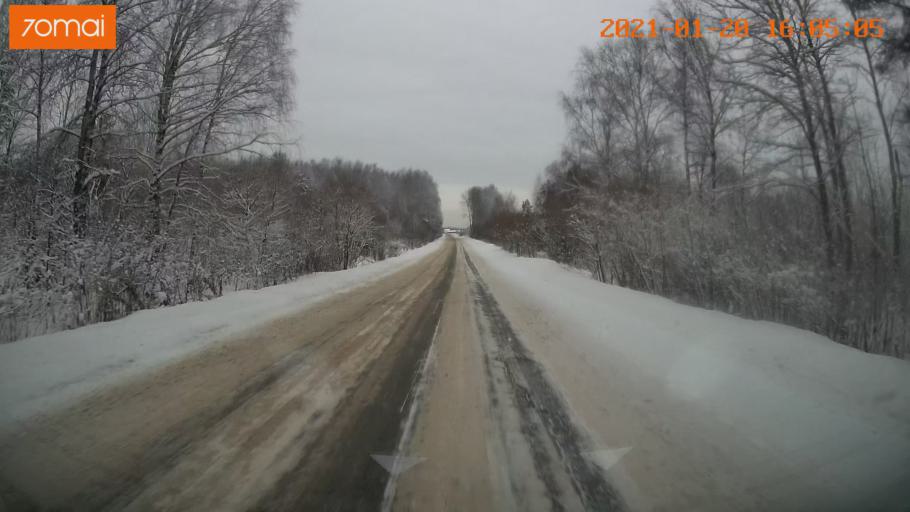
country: RU
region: Vladimir
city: Sudogda
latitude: 56.0624
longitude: 40.8104
